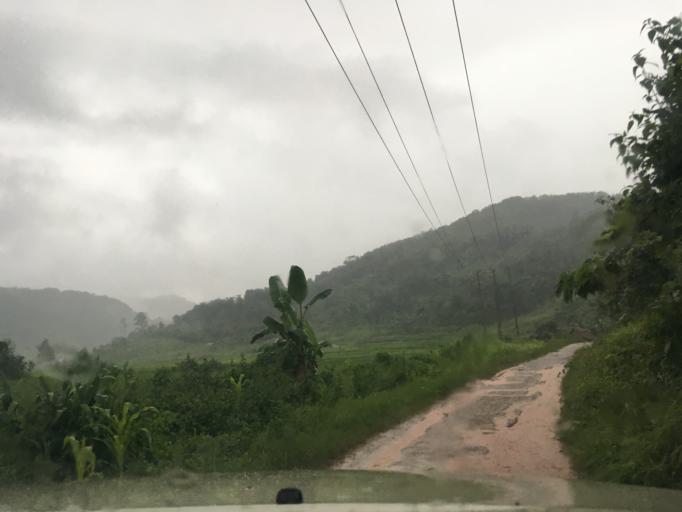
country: LA
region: Oudomxai
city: Muang La
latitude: 21.2402
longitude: 101.9518
